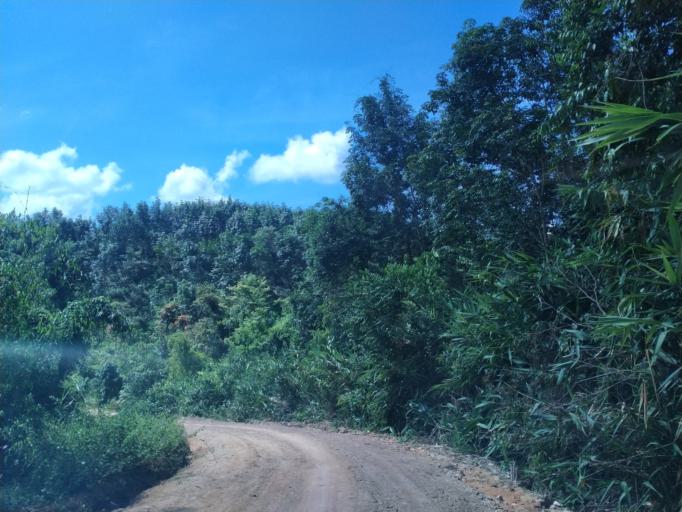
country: LA
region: Vientiane
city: Muang Phon-Hong
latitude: 18.6386
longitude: 102.8864
